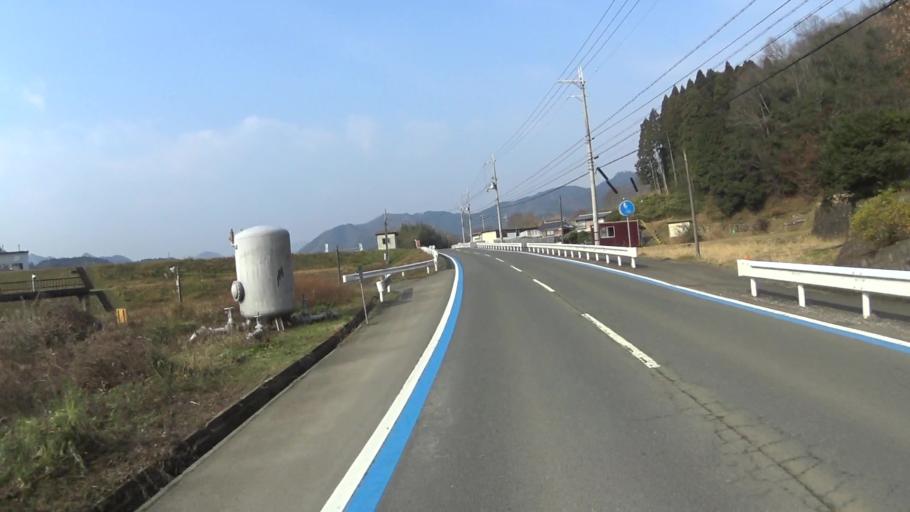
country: JP
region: Kyoto
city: Fukuchiyama
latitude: 35.3317
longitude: 135.1179
